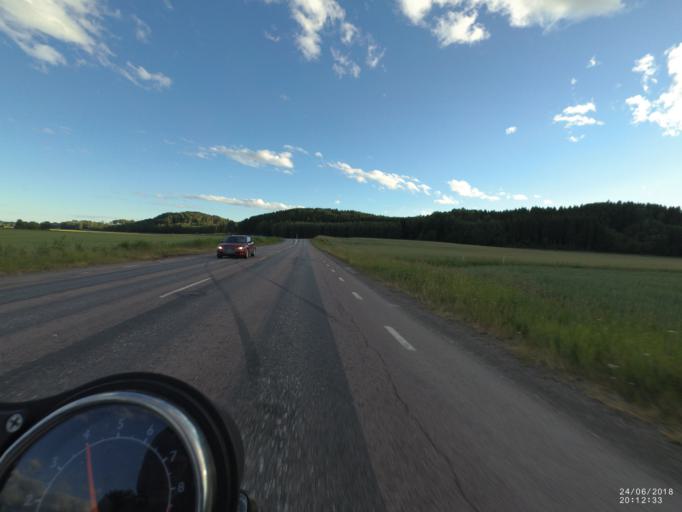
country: SE
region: Soedermanland
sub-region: Nykopings Kommun
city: Nykoping
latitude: 58.8155
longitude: 17.0852
